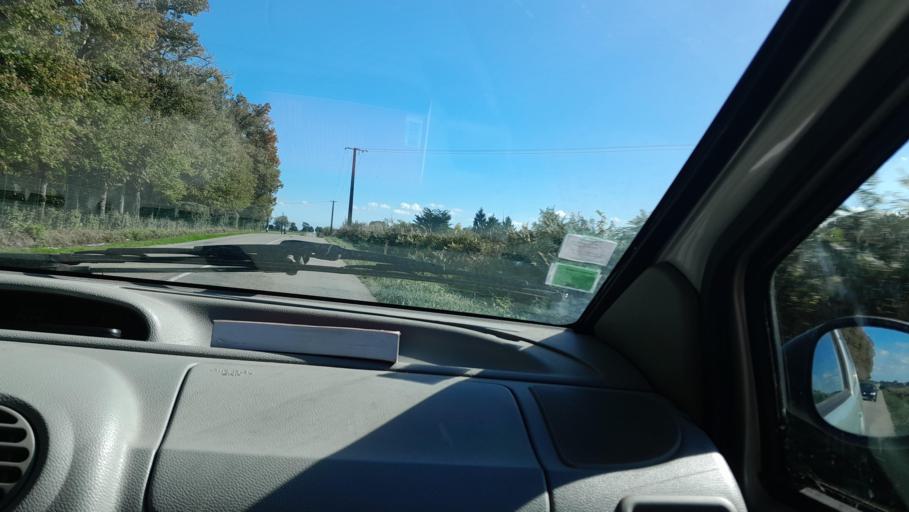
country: FR
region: Pays de la Loire
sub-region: Departement de la Mayenne
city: Quelaines-Saint-Gault
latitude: 47.9357
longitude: -0.8555
